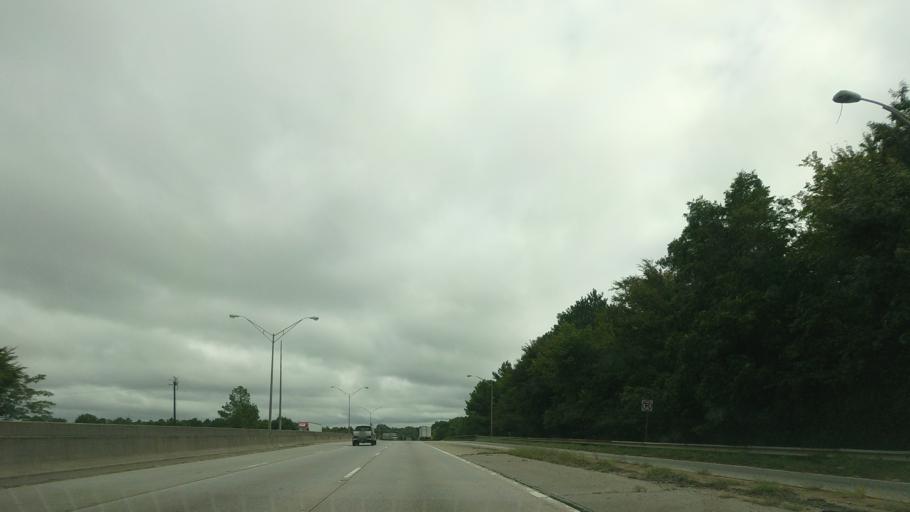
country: US
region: Georgia
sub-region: Bibb County
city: Macon
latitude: 32.7902
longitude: -83.6671
